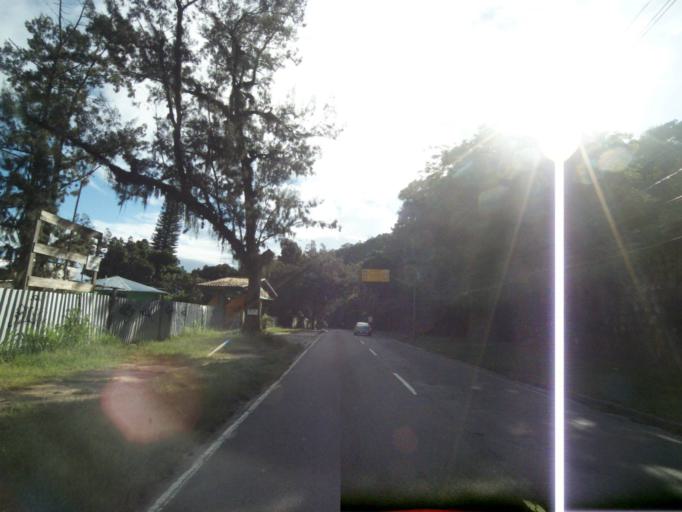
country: BR
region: Rio de Janeiro
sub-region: Rio De Janeiro
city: Rio de Janeiro
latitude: -22.9271
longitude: -43.3179
